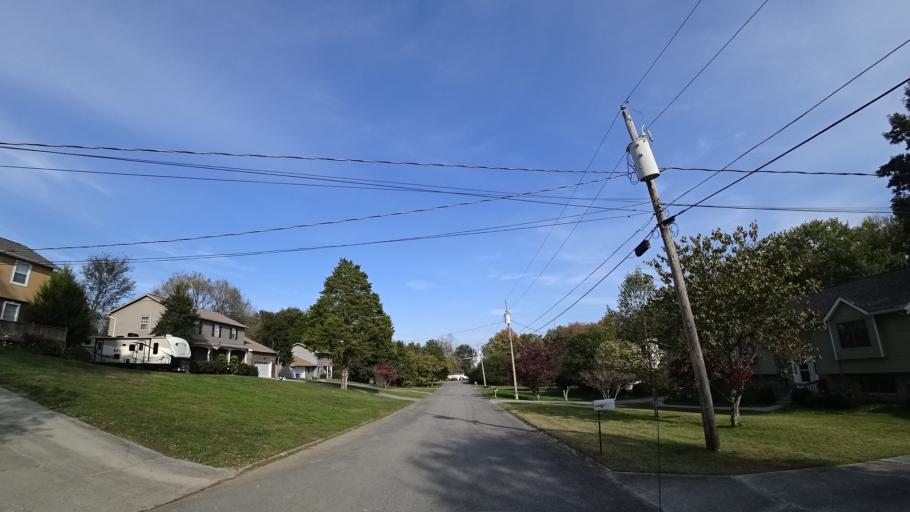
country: US
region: Tennessee
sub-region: Knox County
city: Farragut
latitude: 35.9068
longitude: -84.1591
